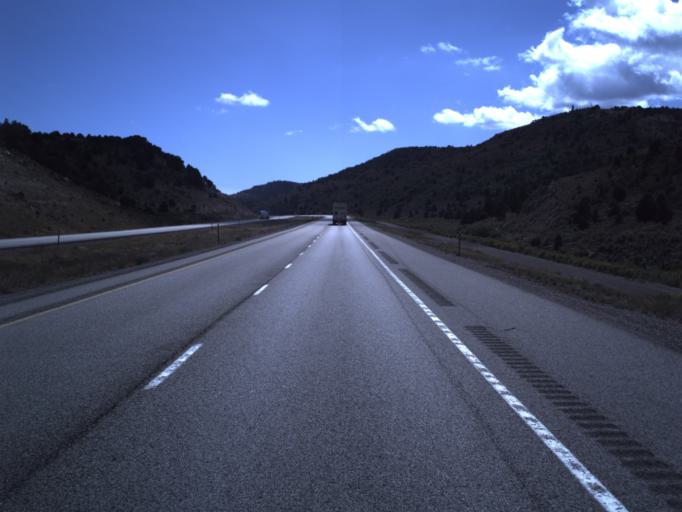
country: US
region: Utah
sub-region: Sevier County
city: Salina
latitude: 38.7937
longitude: -111.5070
